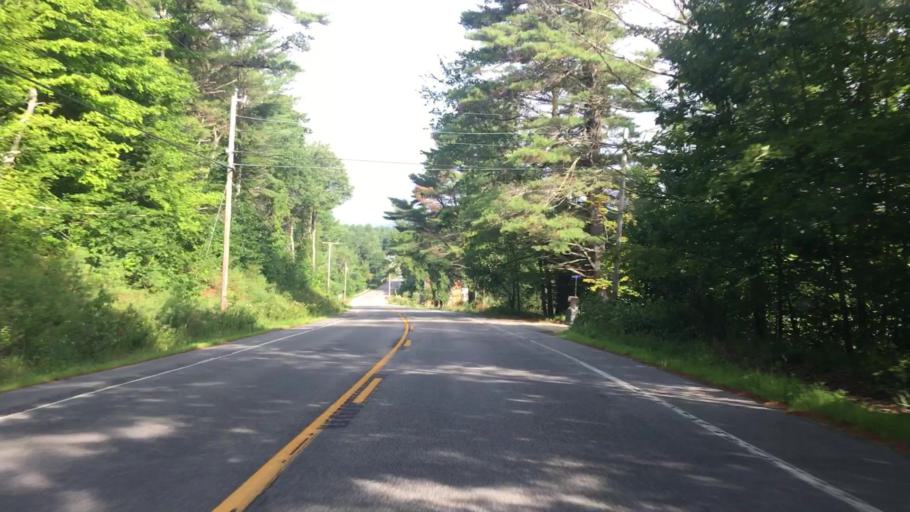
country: US
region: Maine
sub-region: York County
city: Cornish
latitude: 43.7859
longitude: -70.7622
